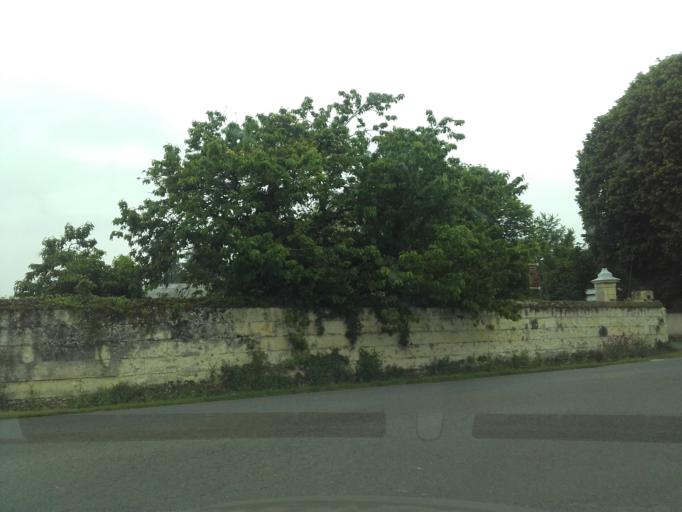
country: FR
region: Pays de la Loire
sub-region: Departement de la Sarthe
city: Ruille-sur-Loir
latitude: 47.7521
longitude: 0.6849
